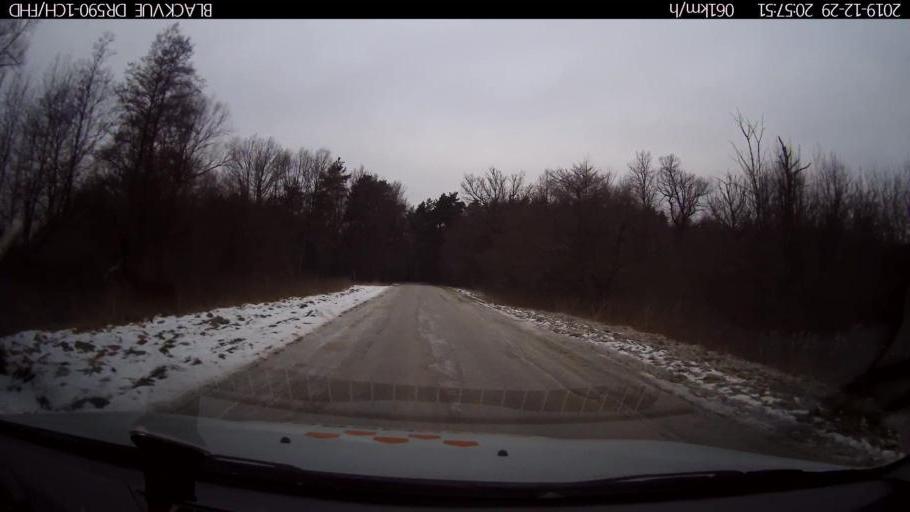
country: RU
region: Nizjnij Novgorod
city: Afonino
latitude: 56.1646
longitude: 43.9893
